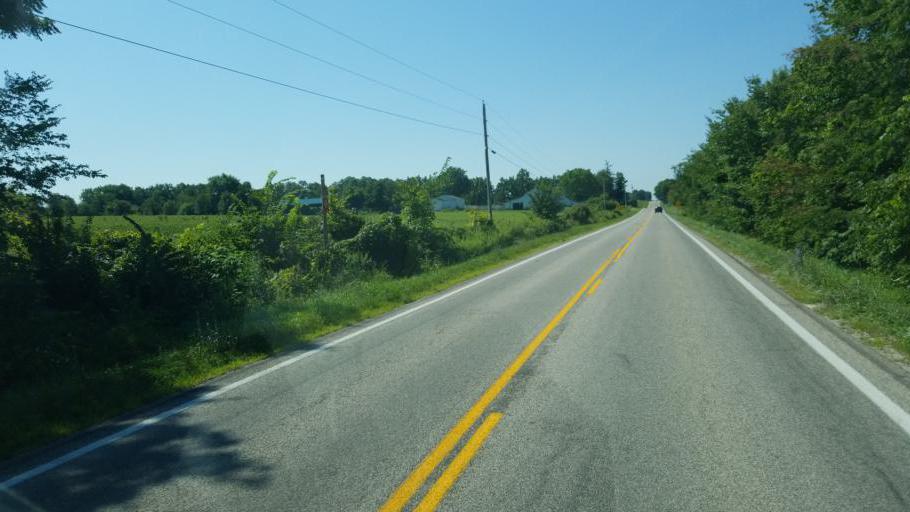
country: US
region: Ohio
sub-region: Morrow County
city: Mount Gilead
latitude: 40.4856
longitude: -82.8204
